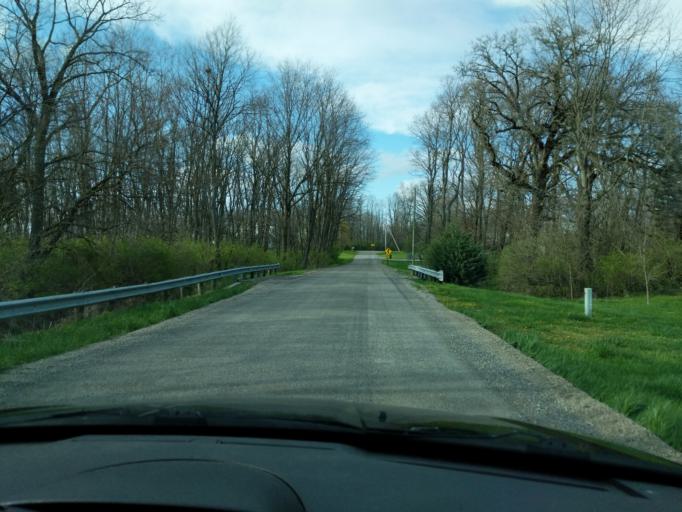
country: US
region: Ohio
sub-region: Champaign County
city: Urbana
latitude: 40.1378
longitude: -83.6883
